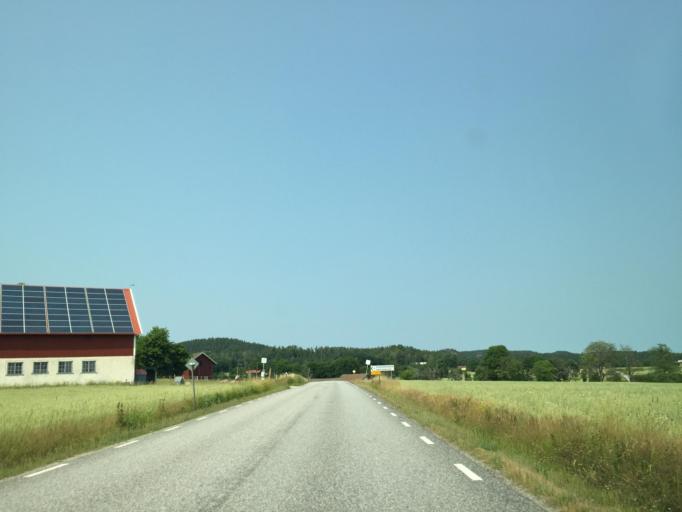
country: SE
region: Vaestra Goetaland
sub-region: Lilla Edets Kommun
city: Lilla Edet
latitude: 58.1961
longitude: 12.1178
